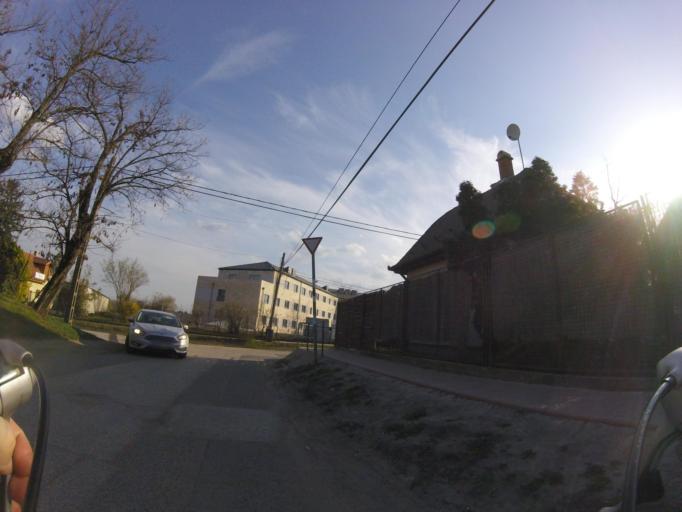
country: HU
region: Pest
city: Diosd
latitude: 47.3879
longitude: 18.9397
